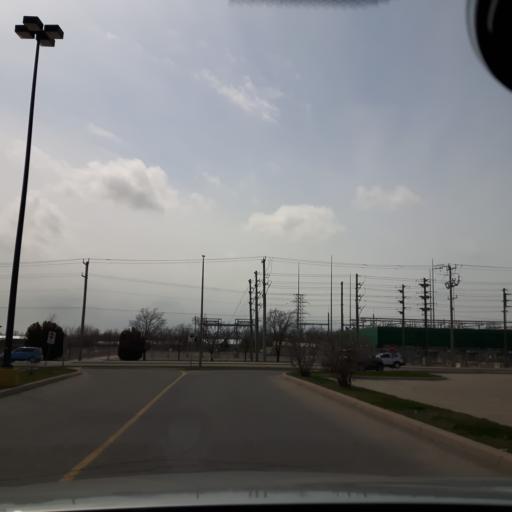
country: CA
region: Ontario
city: Goderich
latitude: 43.7313
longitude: -81.6902
